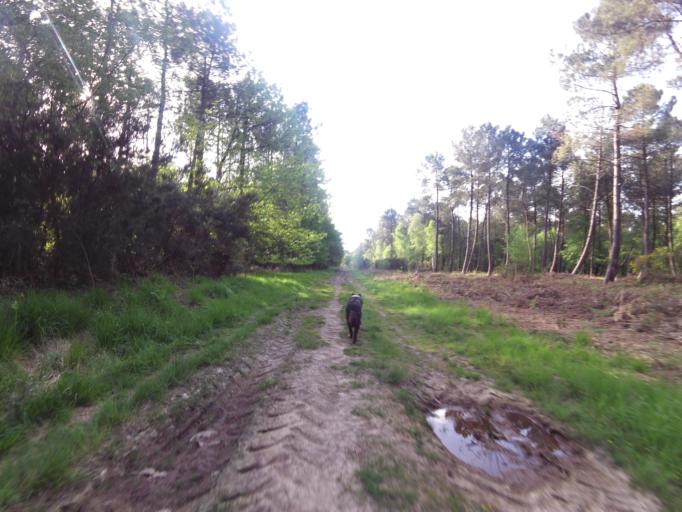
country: FR
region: Brittany
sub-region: Departement du Morbihan
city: Molac
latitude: 47.7382
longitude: -2.4232
